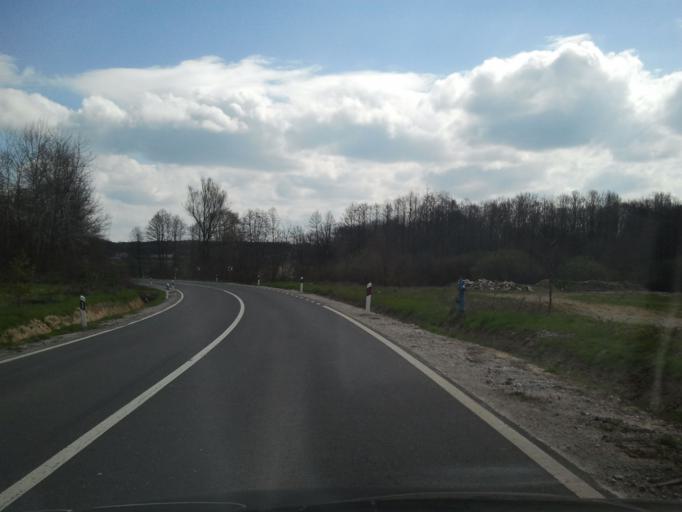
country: HR
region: Grad Zagreb
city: Horvati
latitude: 45.6967
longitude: 15.7582
